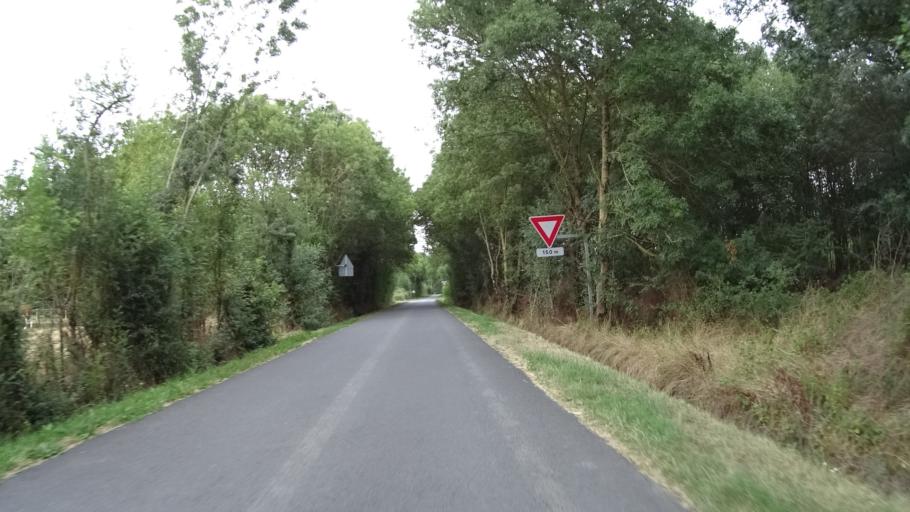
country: FR
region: Pays de la Loire
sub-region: Departement de la Loire-Atlantique
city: Saint-Gereon
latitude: 47.3591
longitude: -1.2117
